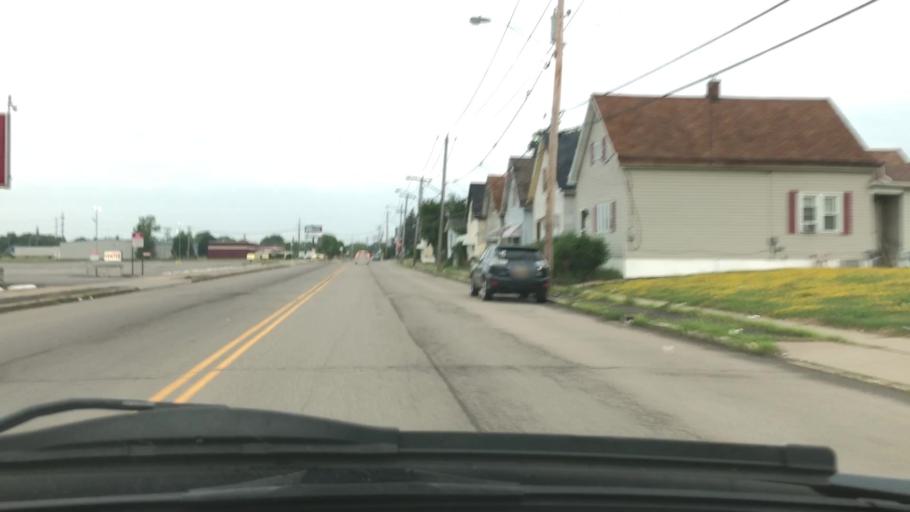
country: US
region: New York
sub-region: Erie County
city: Sloan
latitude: 42.8797
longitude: -78.8012
